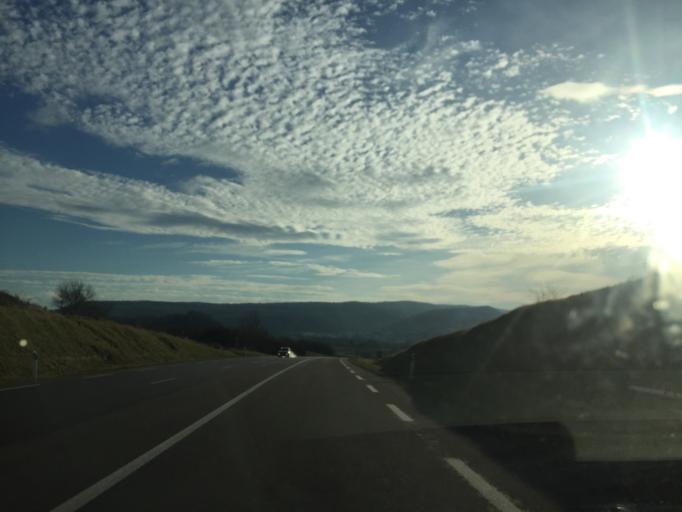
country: FR
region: Franche-Comte
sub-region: Departement du Jura
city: Arbois
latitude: 46.9292
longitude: 5.7758
